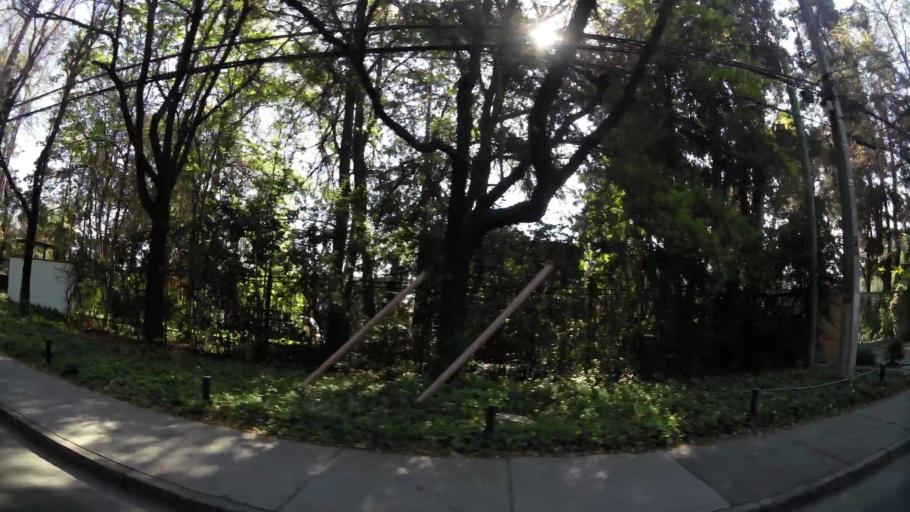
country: CL
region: Santiago Metropolitan
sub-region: Provincia de Santiago
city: Villa Presidente Frei, Nunoa, Santiago, Chile
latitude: -33.3925
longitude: -70.5216
